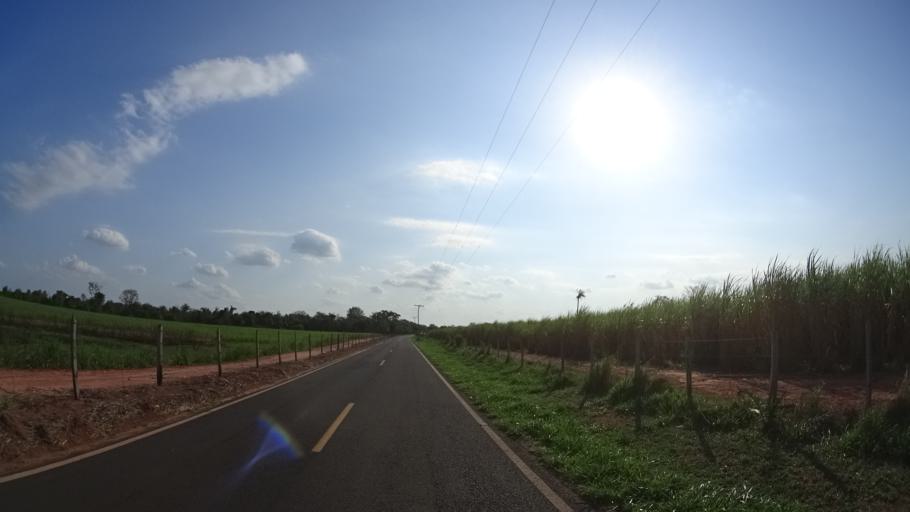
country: BR
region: Sao Paulo
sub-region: Urupes
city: Urupes
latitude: -21.3930
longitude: -49.5075
